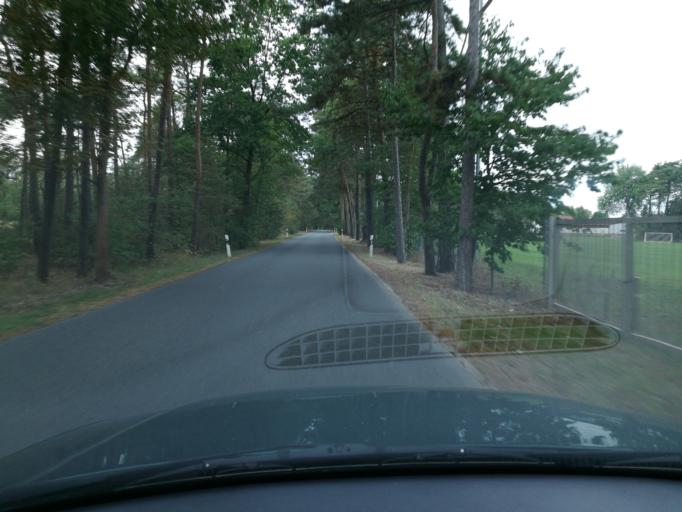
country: DE
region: Bavaria
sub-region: Regierungsbezirk Mittelfranken
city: Furth
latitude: 49.5049
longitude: 10.9874
